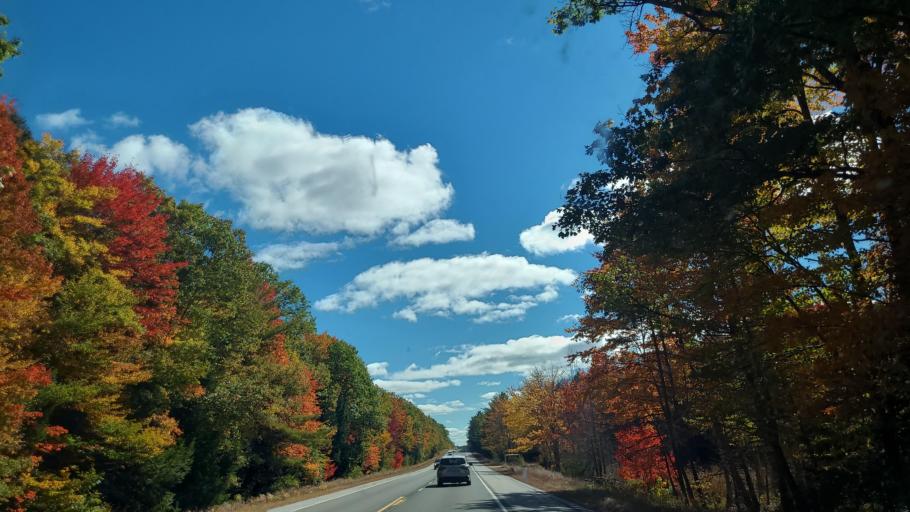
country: US
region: Maine
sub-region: Cumberland County
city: Bridgton
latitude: 44.0072
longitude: -70.6737
